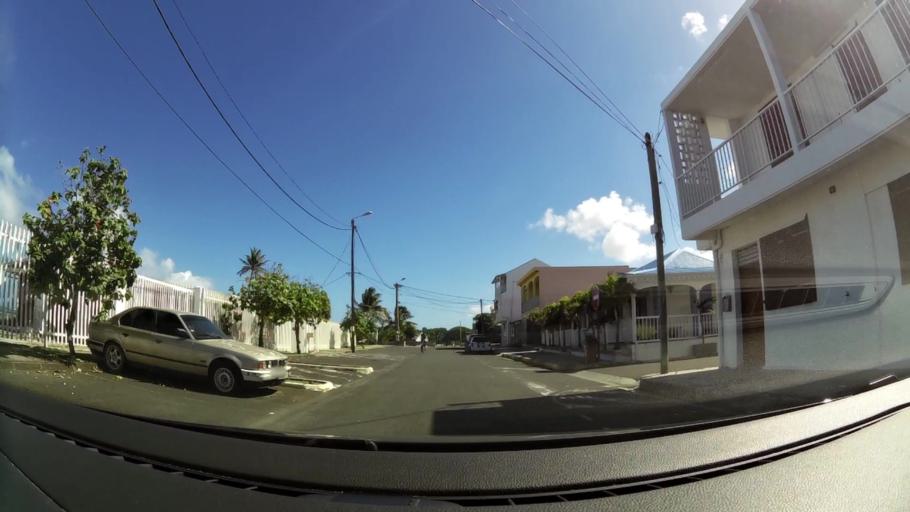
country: GP
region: Guadeloupe
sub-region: Guadeloupe
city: Le Moule
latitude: 16.3323
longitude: -61.3437
